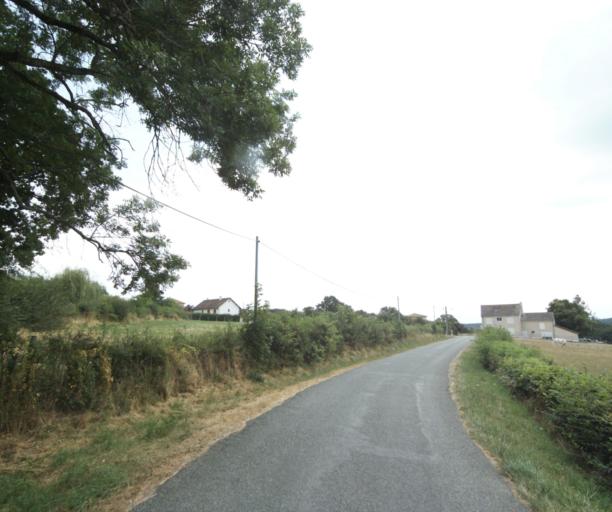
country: FR
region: Bourgogne
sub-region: Departement de Saone-et-Loire
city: Gueugnon
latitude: 46.6028
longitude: 4.0113
